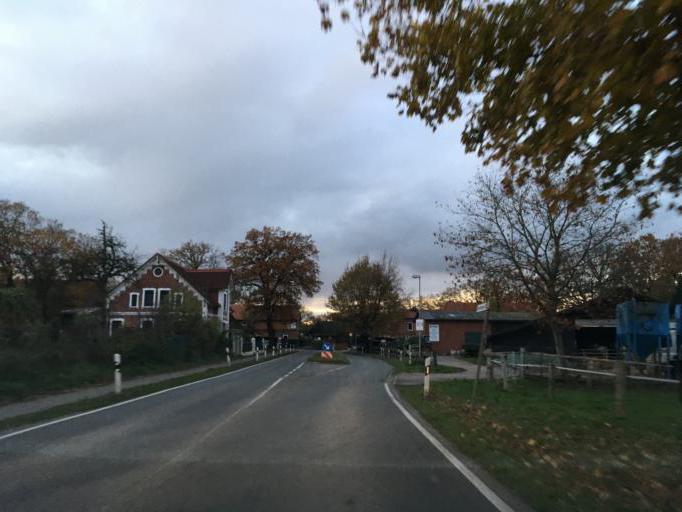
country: DE
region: Lower Saxony
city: Stelle
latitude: 53.3602
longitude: 10.1385
